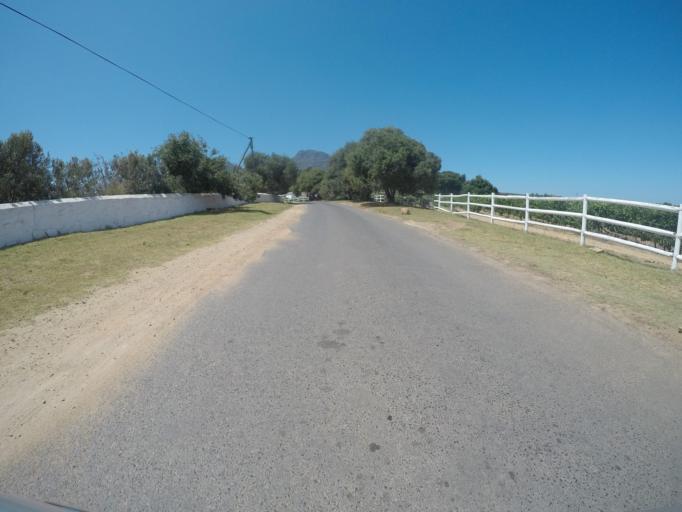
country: ZA
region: Western Cape
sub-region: Cape Winelands District Municipality
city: Stellenbosch
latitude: -33.9929
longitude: 18.8684
